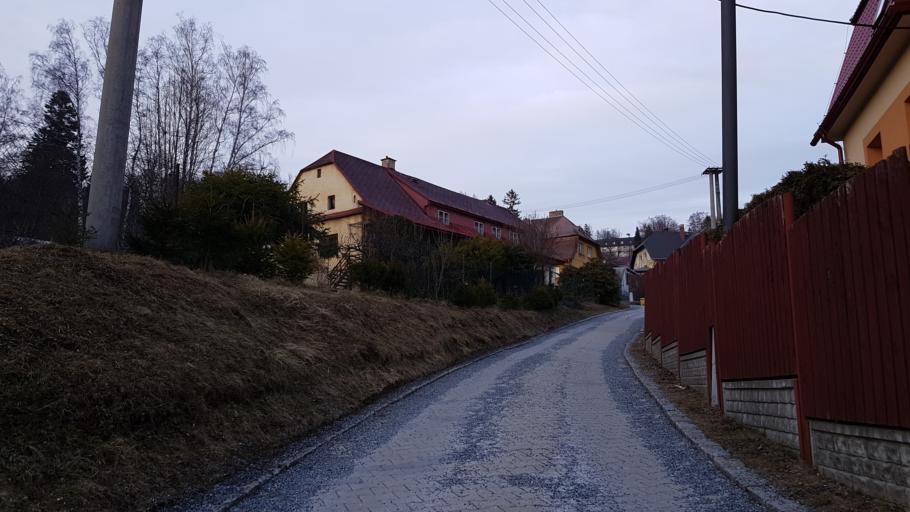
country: CZ
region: Olomoucky
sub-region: Okres Jesenik
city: Jesenik
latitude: 50.2365
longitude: 17.1861
